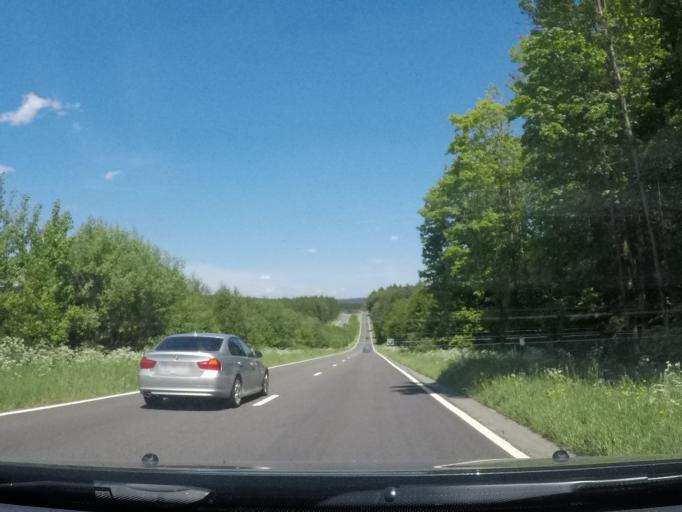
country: BE
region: Wallonia
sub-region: Province du Luxembourg
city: Saint-Hubert
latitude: 49.9558
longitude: 5.3583
